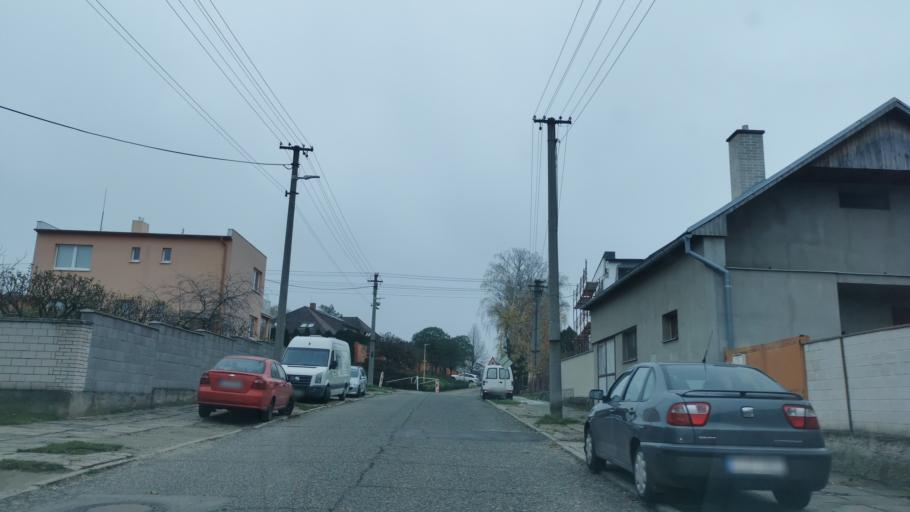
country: SK
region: Trnavsky
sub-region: Okres Skalica
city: Holic
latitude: 48.8162
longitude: 17.1690
